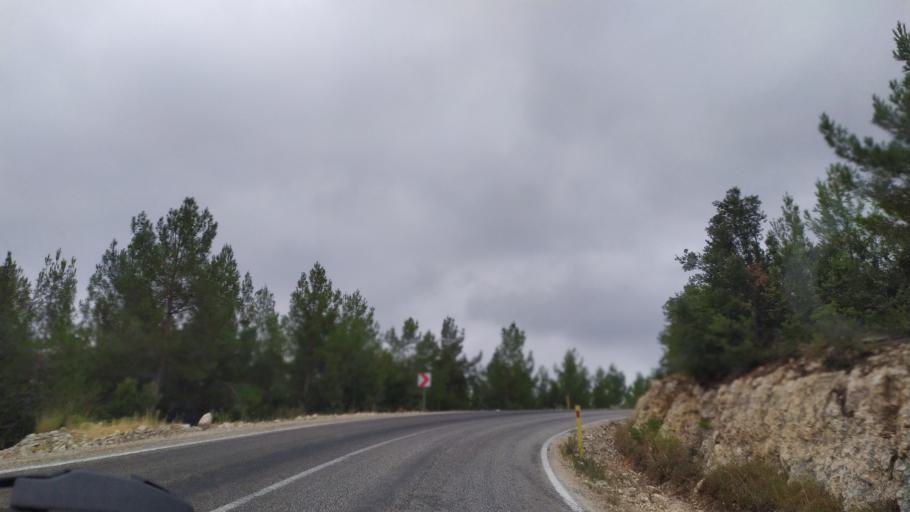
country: TR
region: Mersin
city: Silifke
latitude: 36.5411
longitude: 33.9300
